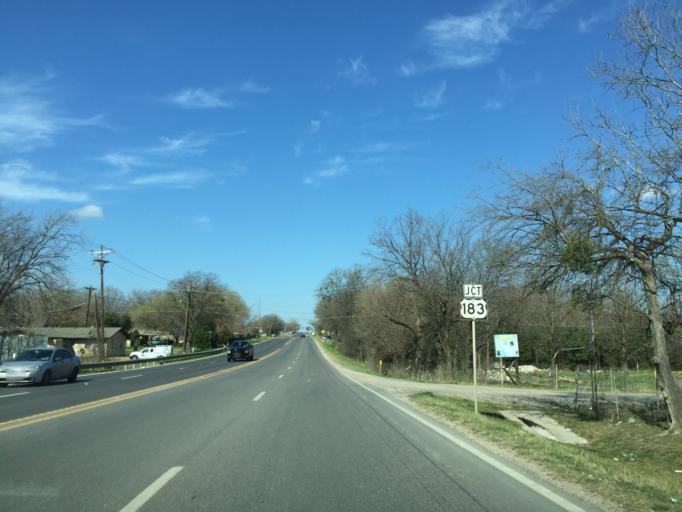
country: US
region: Texas
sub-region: Travis County
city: Onion Creek
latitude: 30.1620
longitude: -97.6882
